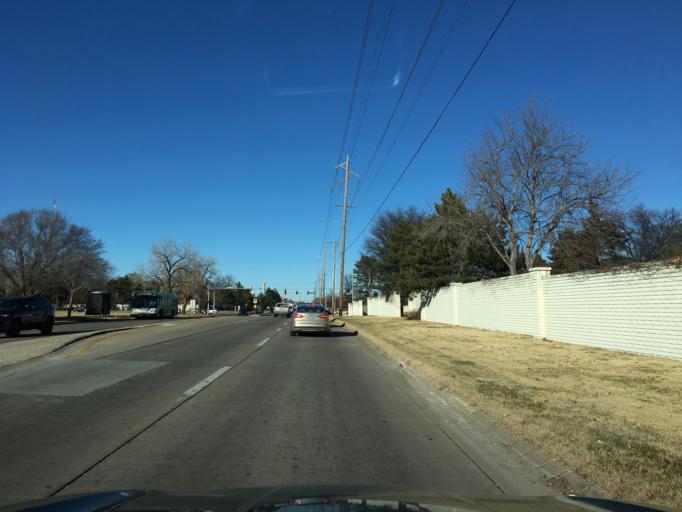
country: US
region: Kansas
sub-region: Sedgwick County
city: Bellaire
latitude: 37.7070
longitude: -97.2446
